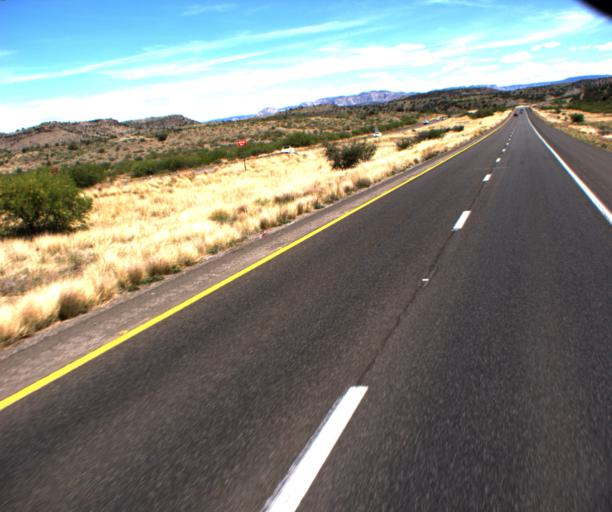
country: US
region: Arizona
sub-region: Yavapai County
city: Cornville
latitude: 34.7783
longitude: -111.9279
